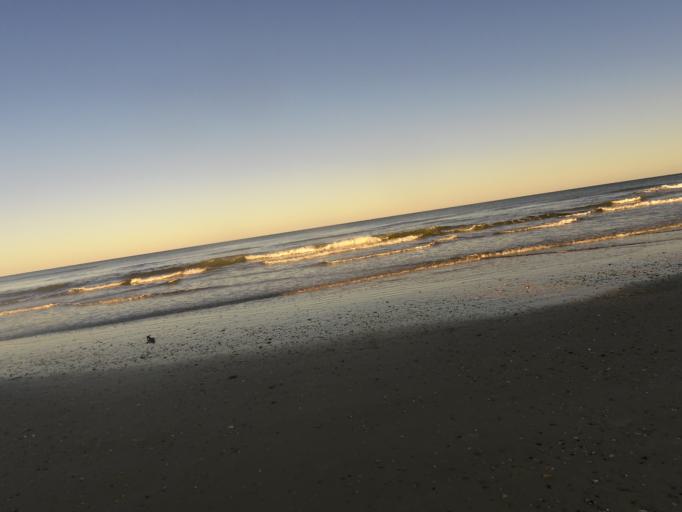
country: US
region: Florida
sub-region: Duval County
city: Atlantic Beach
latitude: 30.4658
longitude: -81.4121
